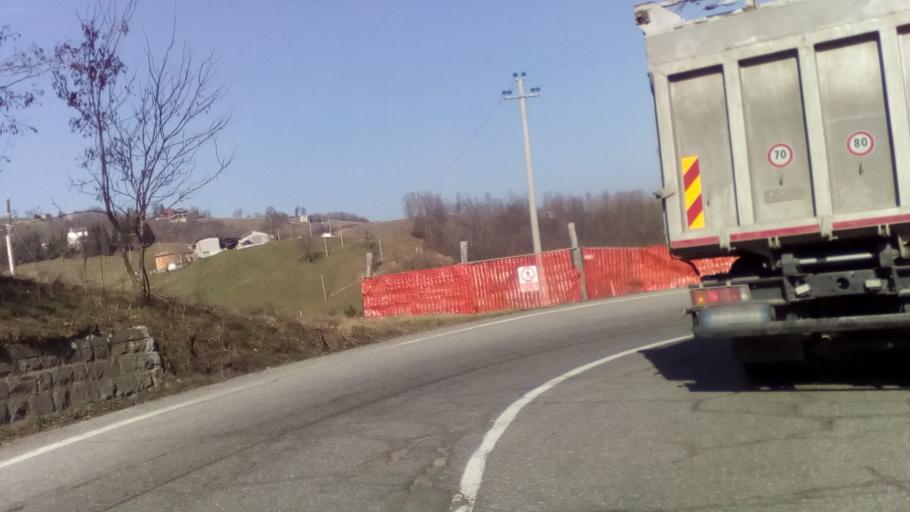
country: IT
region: Emilia-Romagna
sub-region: Provincia di Modena
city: Lama
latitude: 44.3111
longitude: 10.7490
